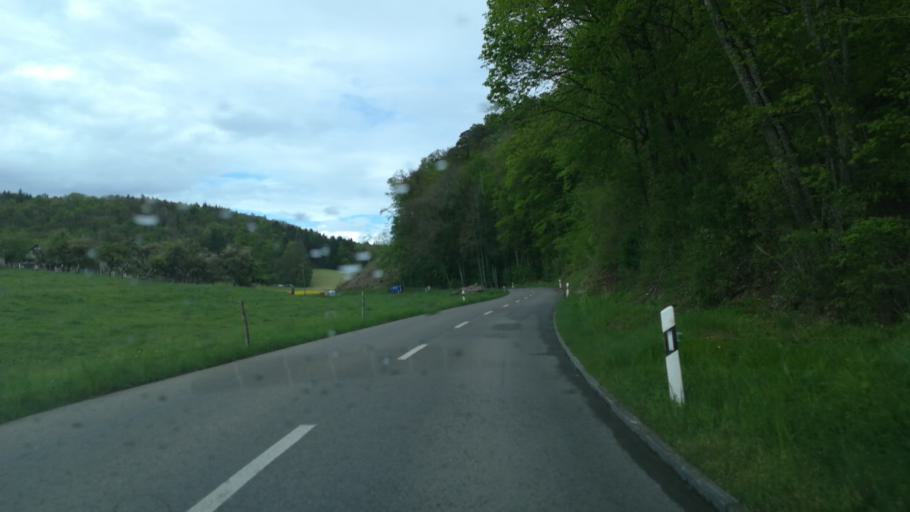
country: CH
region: Schaffhausen
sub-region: Bezirk Reiat
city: Stetten
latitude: 47.7332
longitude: 8.6384
